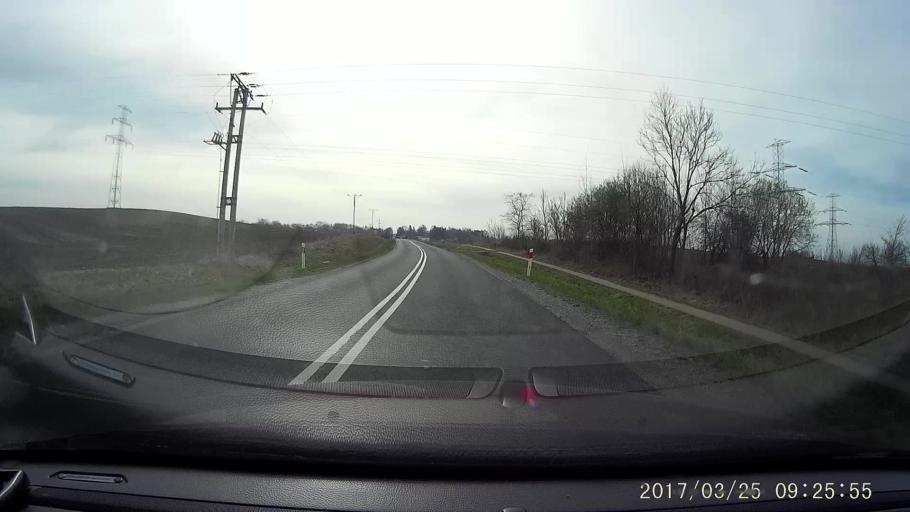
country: PL
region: Silesian Voivodeship
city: Zawidow
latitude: 51.0370
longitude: 15.0486
